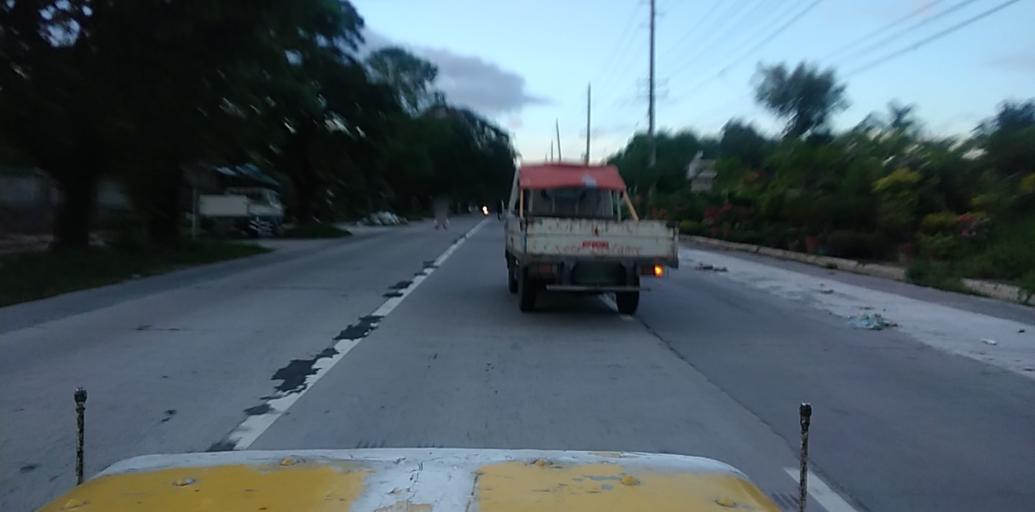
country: PH
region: Central Luzon
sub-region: Province of Pampanga
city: Calibutbut
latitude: 15.1196
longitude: 120.5895
